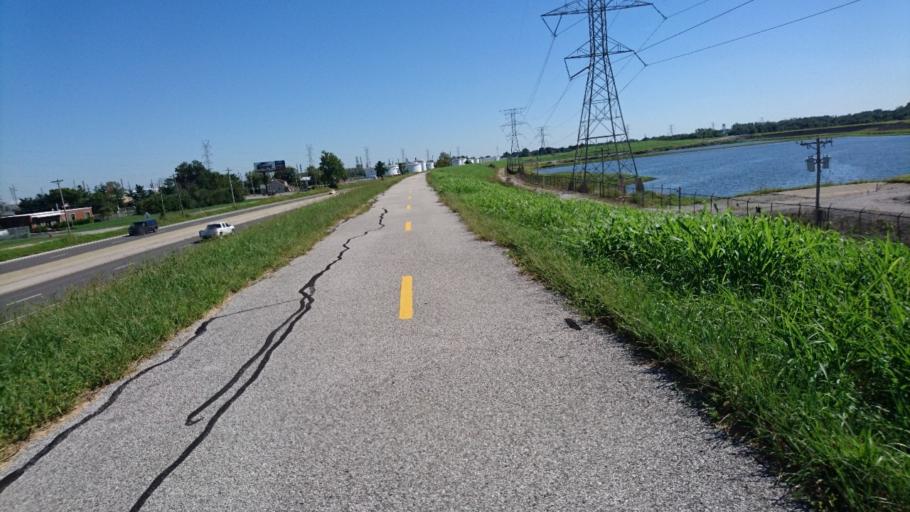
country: US
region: Illinois
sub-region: Madison County
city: Wood River
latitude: 38.8514
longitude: -90.1027
